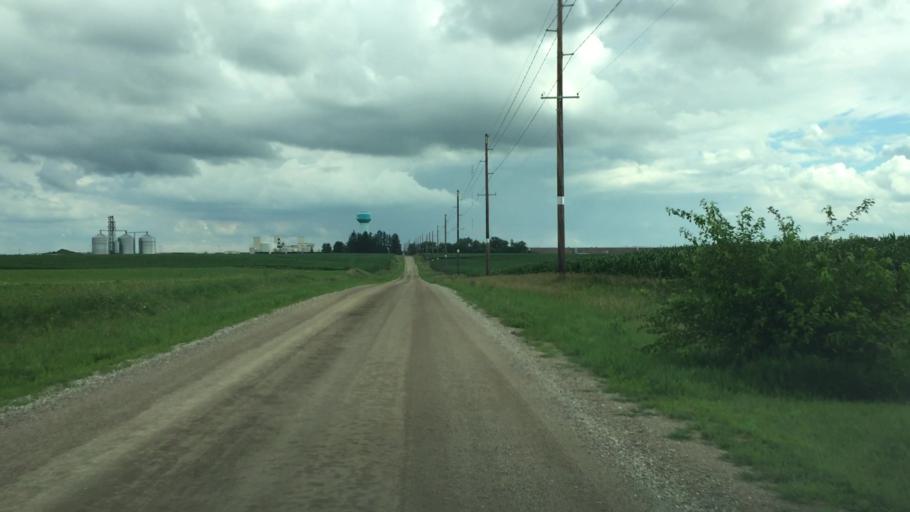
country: US
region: Iowa
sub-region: Jasper County
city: Newton
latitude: 41.7444
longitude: -93.0195
